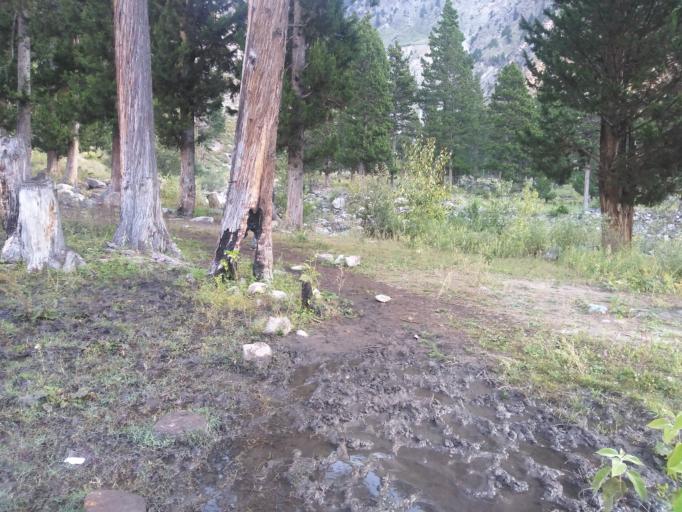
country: NP
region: Western Region
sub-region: Dhawalagiri Zone
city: Jomsom
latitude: 28.8997
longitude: 83.0300
